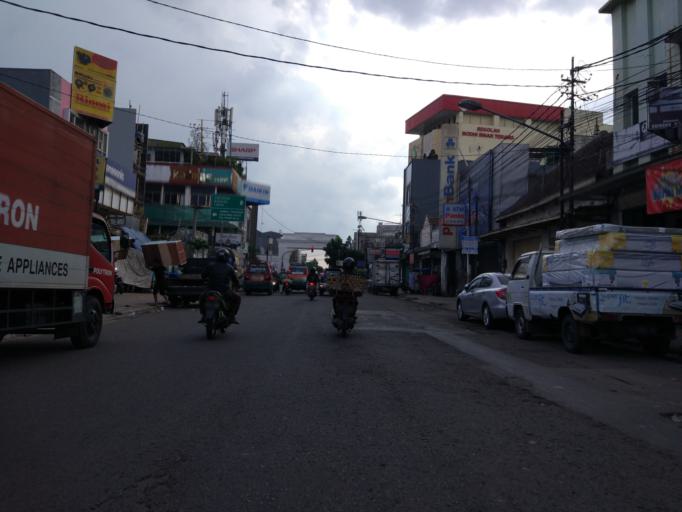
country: ID
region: West Java
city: Bandung
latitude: -6.9188
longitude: 107.5878
